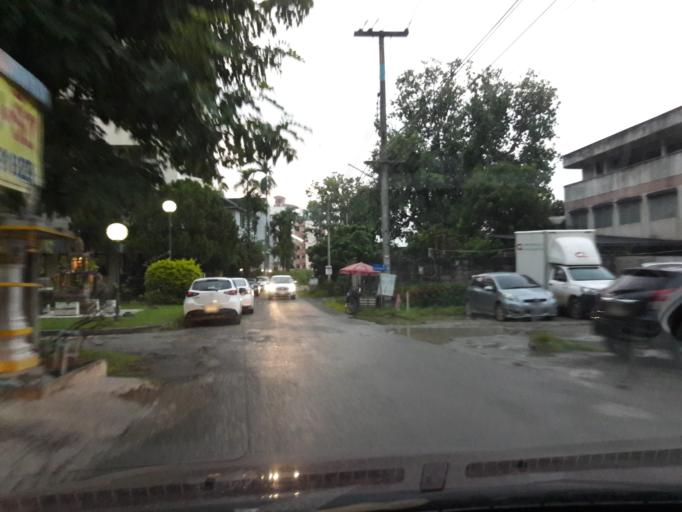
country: TH
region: Chiang Mai
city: Chiang Mai
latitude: 18.7875
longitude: 98.9725
